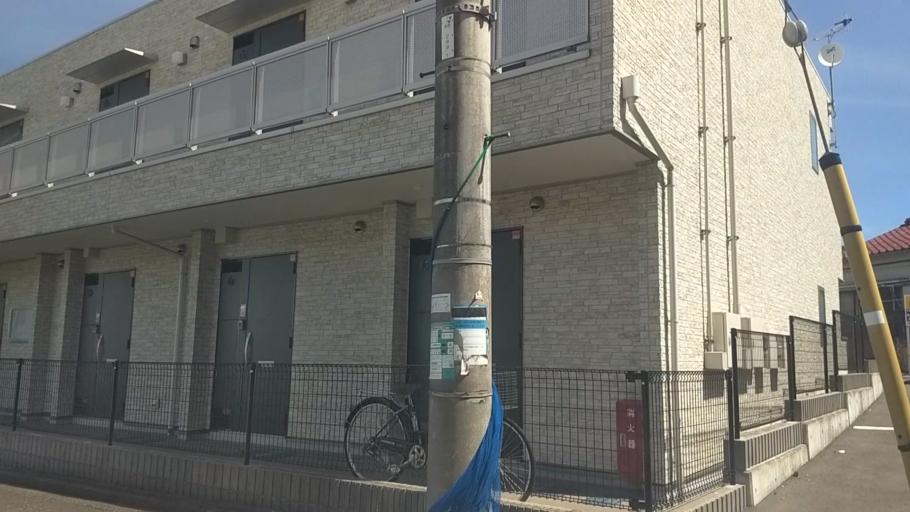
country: JP
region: Kanagawa
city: Yokohama
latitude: 35.4321
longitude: 139.6293
